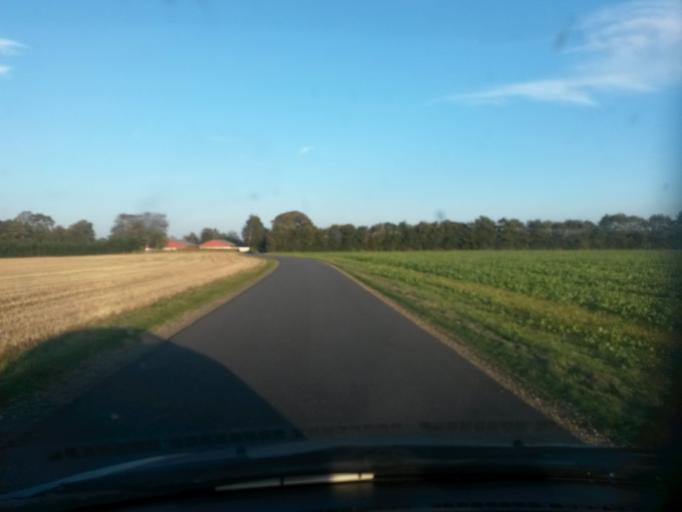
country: DK
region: Central Jutland
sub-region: Ikast-Brande Kommune
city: Bording Kirkeby
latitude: 56.2737
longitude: 9.3079
